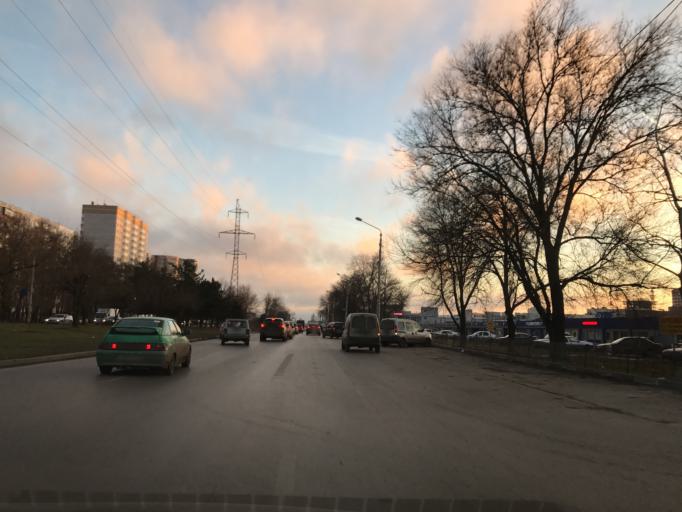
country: RU
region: Rostov
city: Kalinin
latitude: 47.2353
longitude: 39.6135
